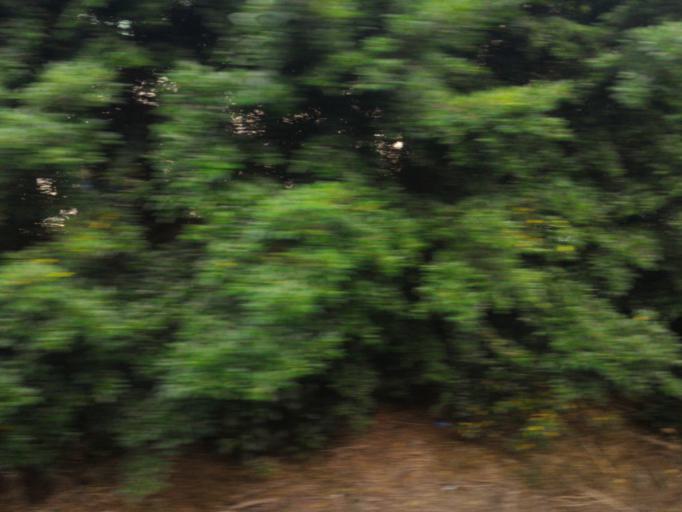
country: TW
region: Taiwan
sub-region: Taoyuan
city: Taoyuan
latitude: 24.9878
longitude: 121.3232
